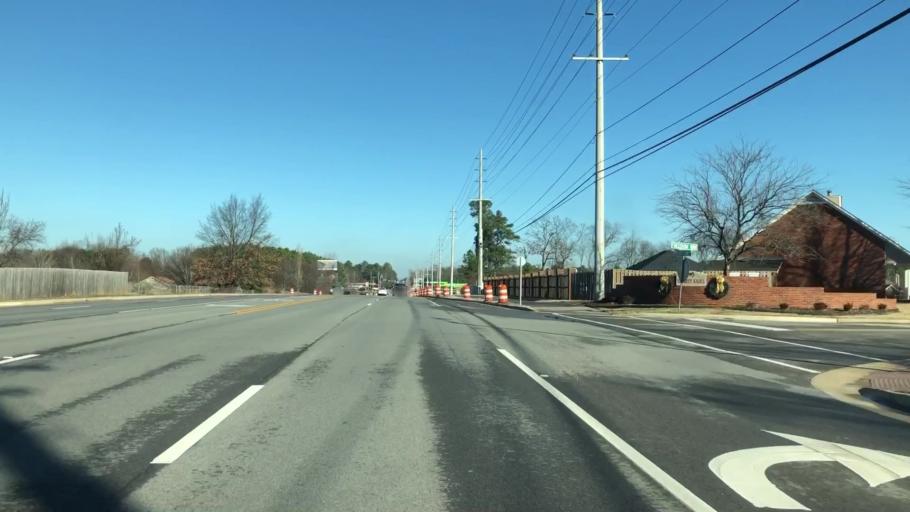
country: US
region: Alabama
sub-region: Madison County
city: Madison
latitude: 34.7419
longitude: -86.7861
